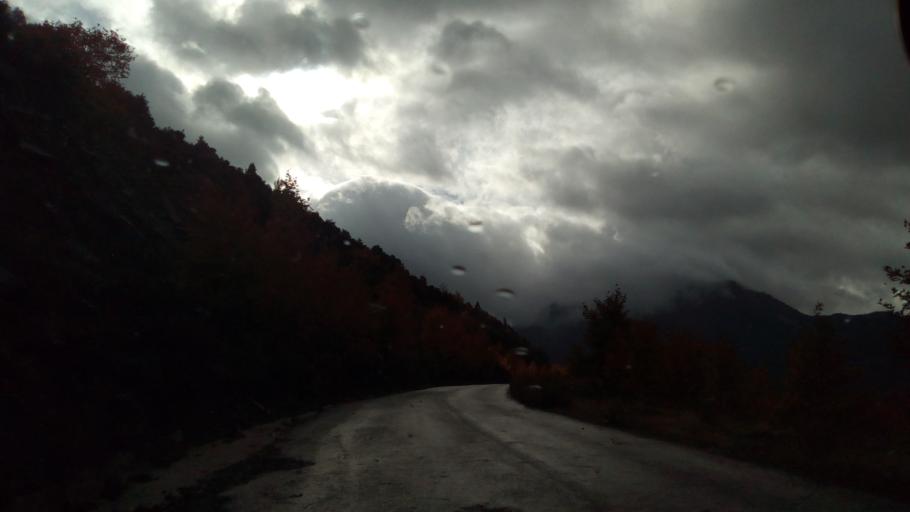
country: GR
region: West Greece
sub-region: Nomos Aitolias kai Akarnanias
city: Thermo
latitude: 38.6782
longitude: 21.8500
